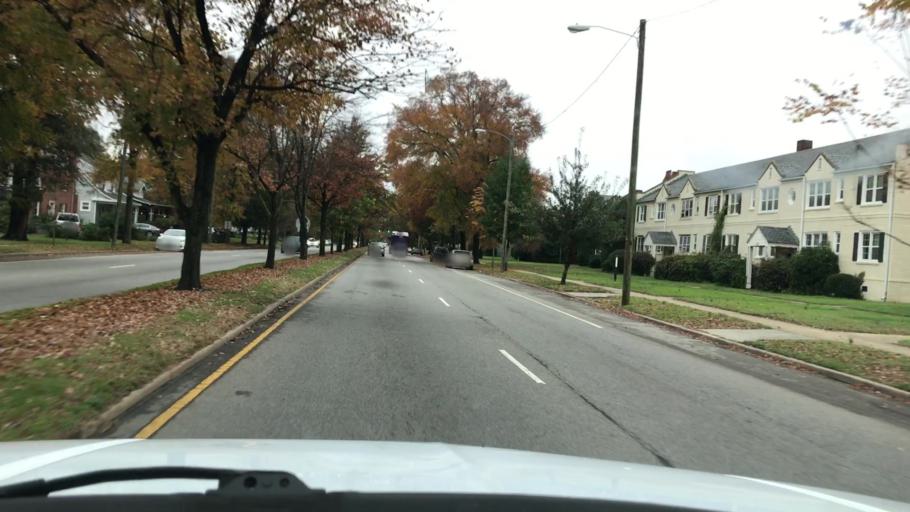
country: US
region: Virginia
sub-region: Henrico County
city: Lakeside
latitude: 37.5948
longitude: -77.4490
